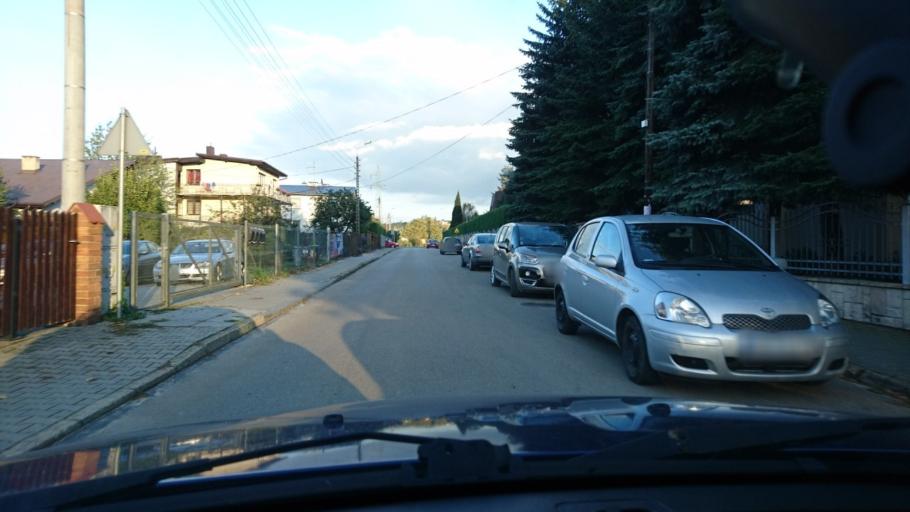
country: PL
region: Silesian Voivodeship
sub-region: Bielsko-Biala
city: Bielsko-Biala
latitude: 49.8424
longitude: 19.0626
